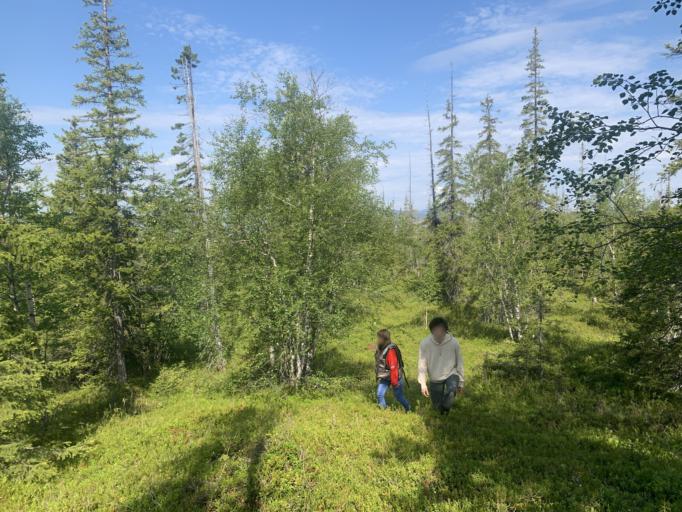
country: RU
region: Murmansk
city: Monchegorsk
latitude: 67.7356
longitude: 33.0700
